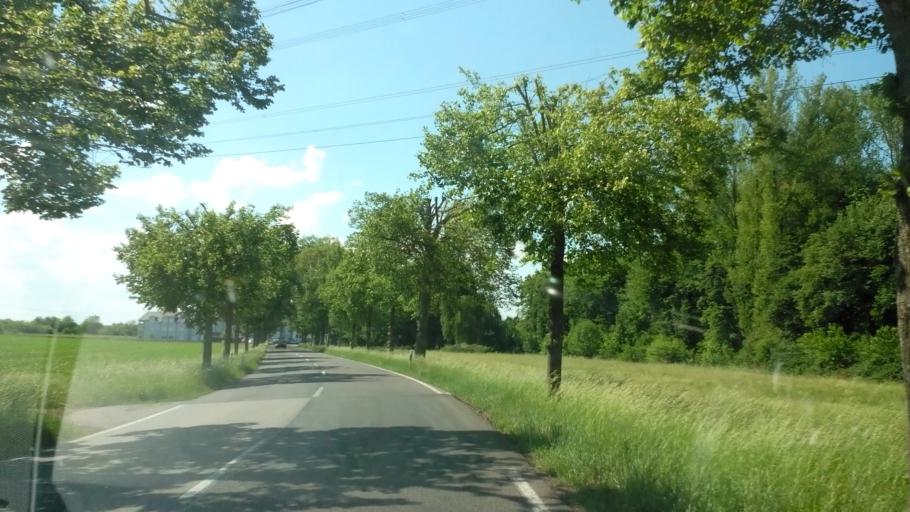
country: DE
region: Saarland
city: Saarwellingen
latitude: 49.3473
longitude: 6.8244
